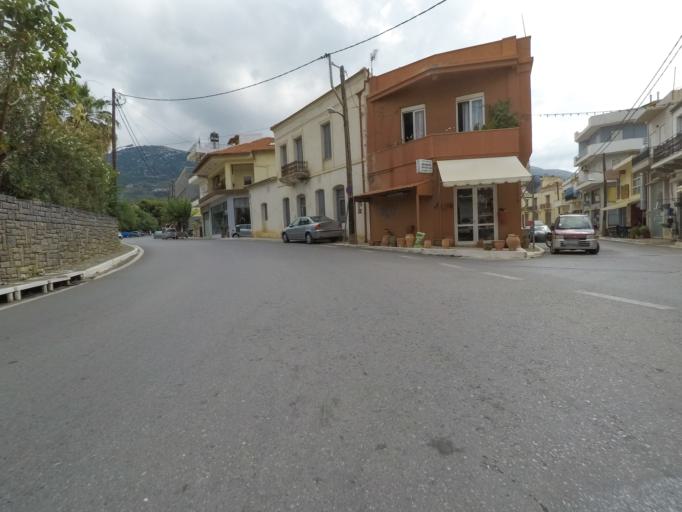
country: GR
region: Crete
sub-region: Nomos Lasithiou
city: Neapoli
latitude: 35.2574
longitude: 25.6076
